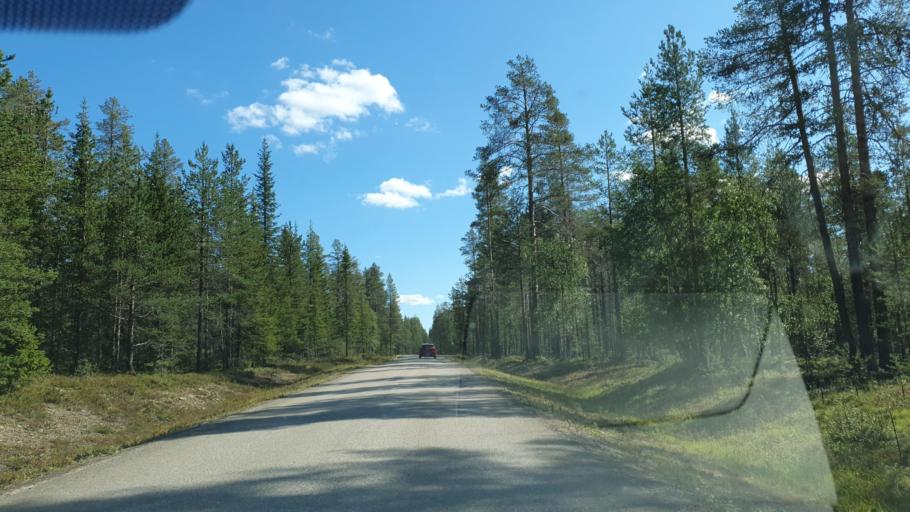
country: FI
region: Lapland
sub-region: Tunturi-Lappi
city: Muonio
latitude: 67.7066
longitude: 24.1377
